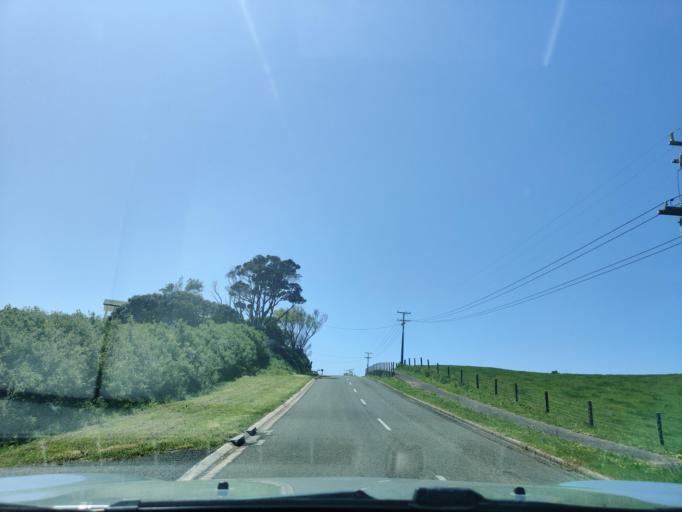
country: NZ
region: Taranaki
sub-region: South Taranaki District
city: Hawera
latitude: -39.6015
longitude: 174.2613
